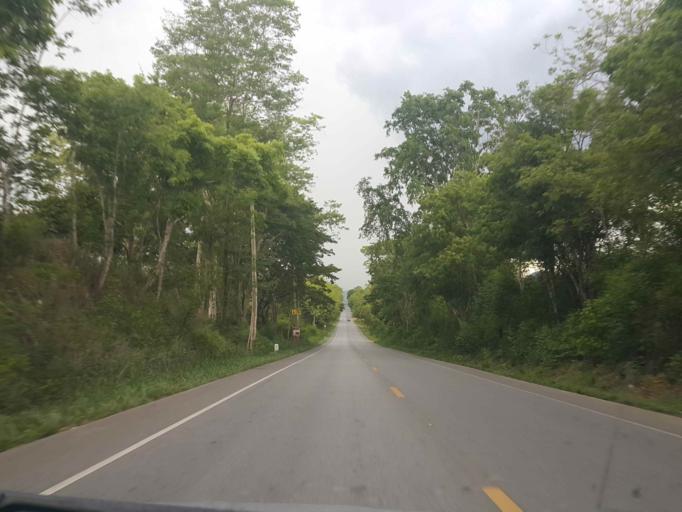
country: TH
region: Phrae
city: Den Chai
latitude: 17.9682
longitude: 100.0492
